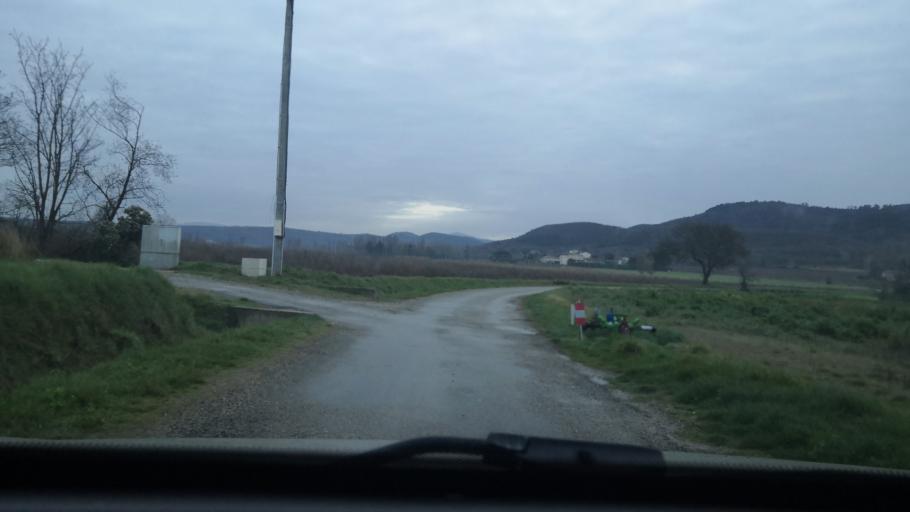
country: FR
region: Rhone-Alpes
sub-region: Departement de la Drome
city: Allan
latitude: 44.5137
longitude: 4.7989
